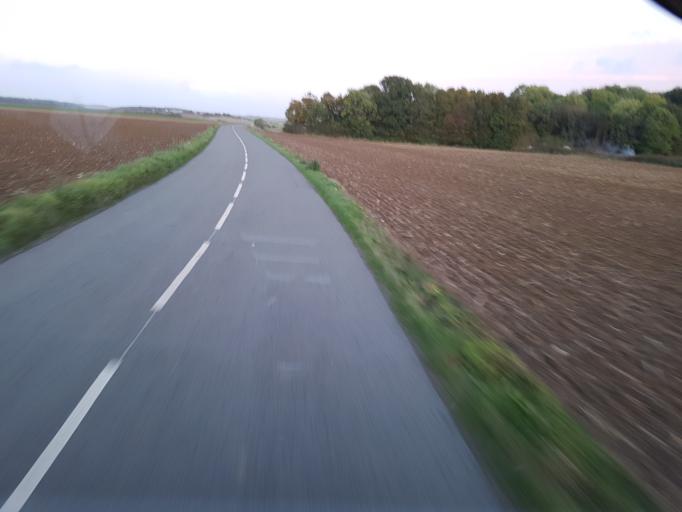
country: FR
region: Picardie
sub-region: Departement de la Somme
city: Ailly-sur-Noye
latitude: 49.7600
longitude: 2.3065
